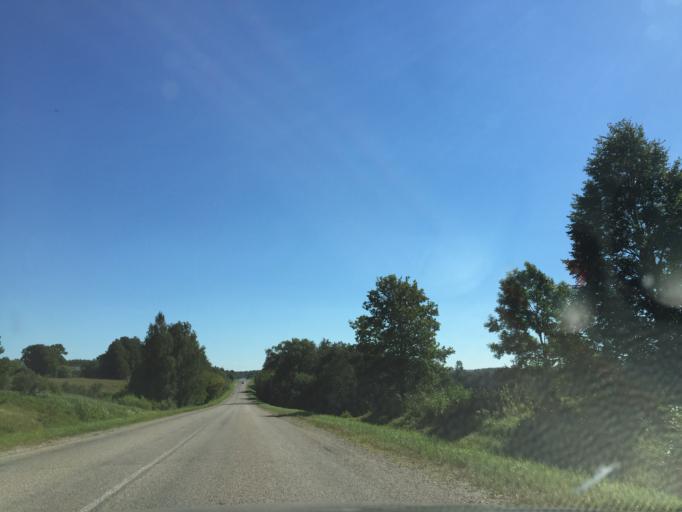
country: LV
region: Akniste
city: Akniste
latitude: 56.0278
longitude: 25.9160
